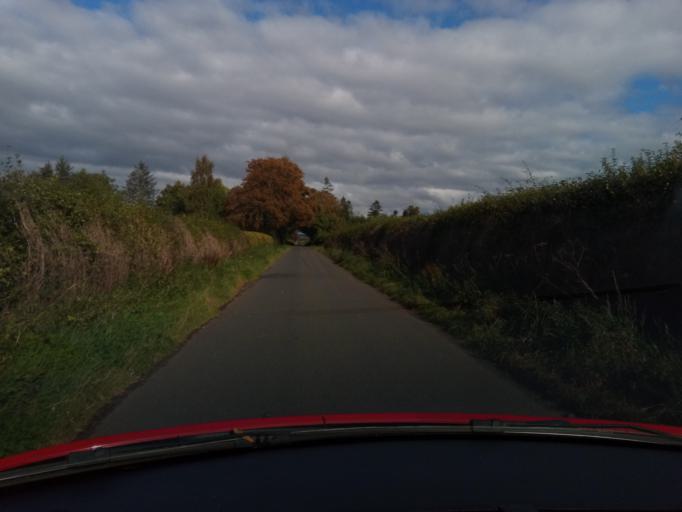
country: GB
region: Scotland
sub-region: The Scottish Borders
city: Kelso
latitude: 55.5613
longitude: -2.4231
